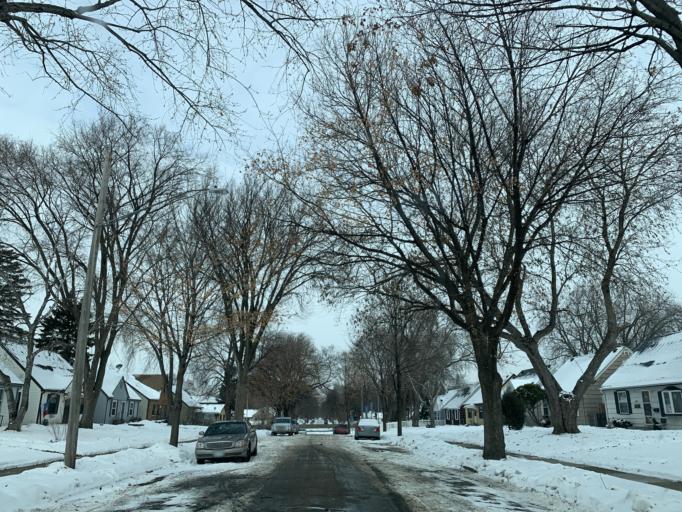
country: US
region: Minnesota
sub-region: Dakota County
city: Mendota Heights
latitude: 44.8968
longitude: -93.2090
